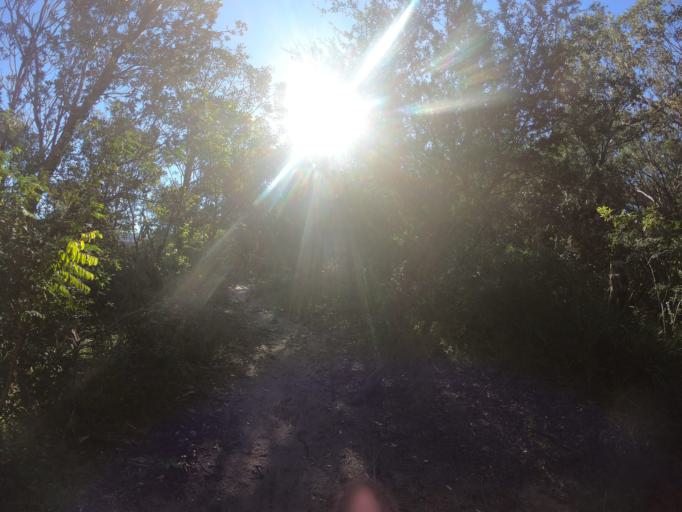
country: AU
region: New South Wales
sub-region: Wollongong
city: Fairy Meadow
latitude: -34.4083
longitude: 150.9010
